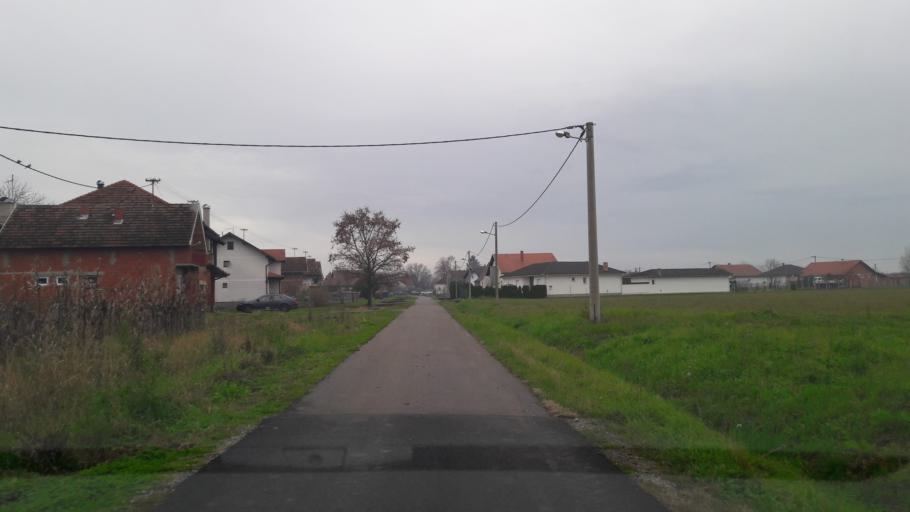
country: HR
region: Osjecko-Baranjska
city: Koska
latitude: 45.5432
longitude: 18.2872
